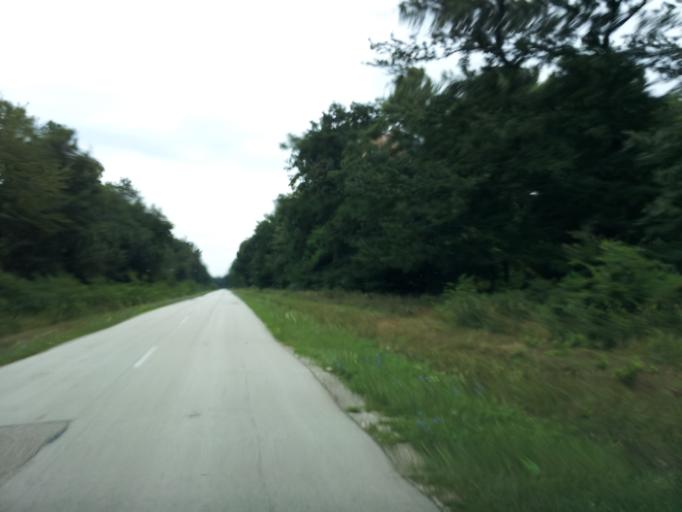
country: HU
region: Vas
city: Vasvar
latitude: 46.9940
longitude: 16.7577
